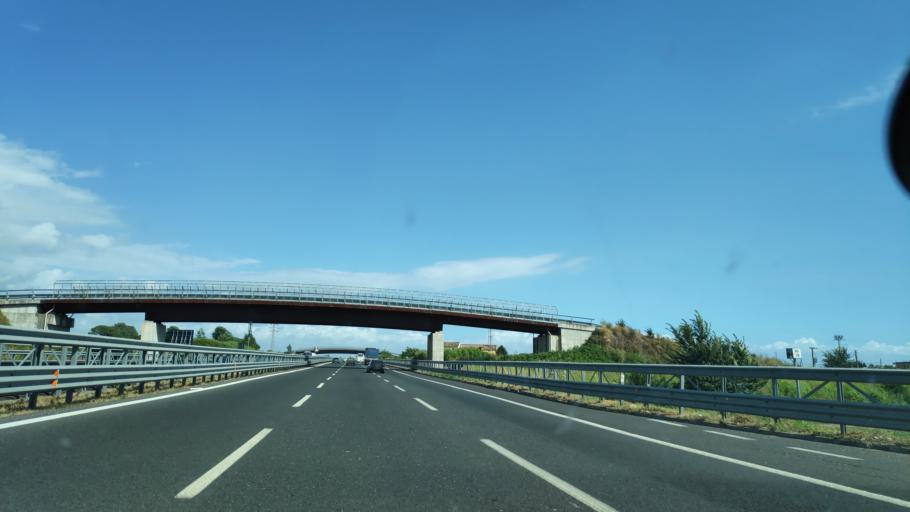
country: IT
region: Campania
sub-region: Provincia di Salerno
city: Pontecagnano
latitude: 40.6504
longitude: 14.8784
